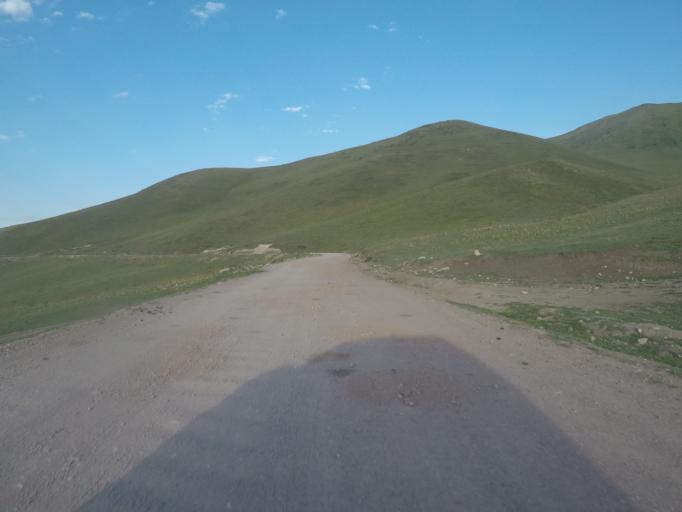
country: KG
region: Chuy
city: Bishkek
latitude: 42.6400
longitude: 74.6398
